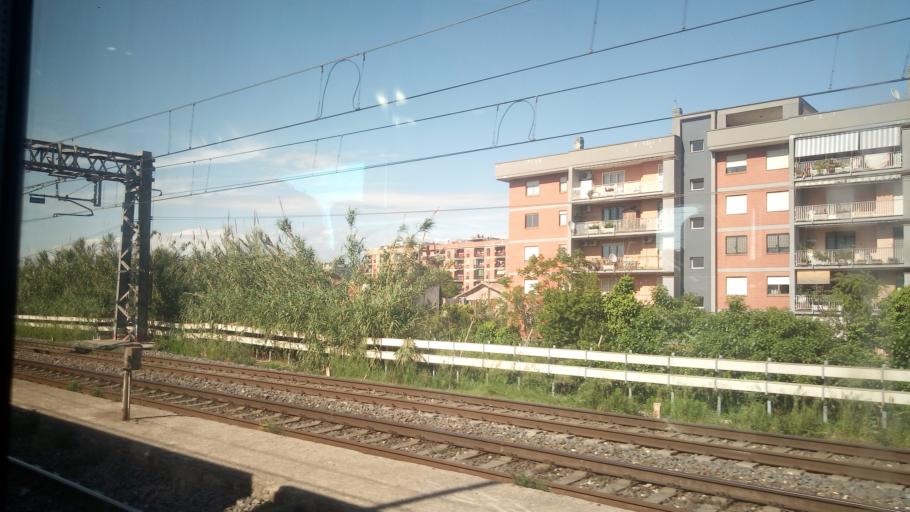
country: IT
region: Latium
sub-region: Citta metropolitana di Roma Capitale
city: Rome
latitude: 41.8741
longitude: 12.5388
